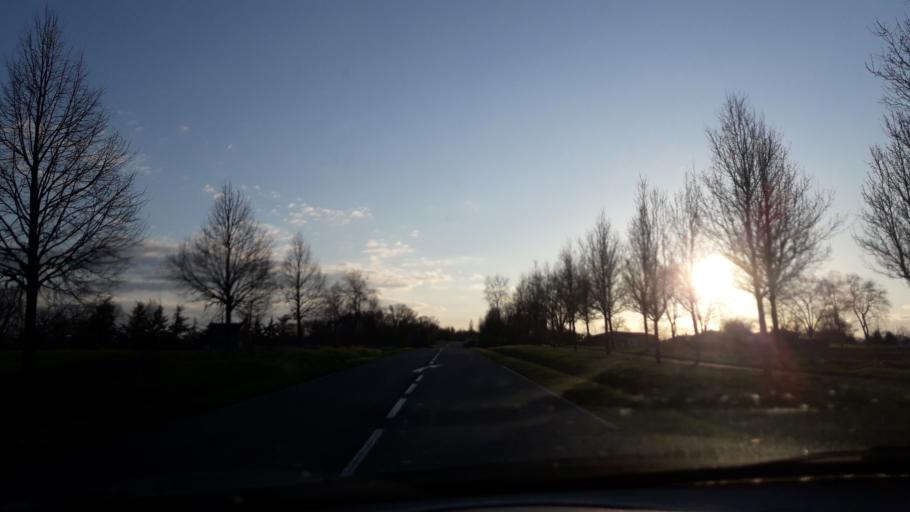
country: FR
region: Midi-Pyrenees
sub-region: Departement de la Haute-Garonne
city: Levignac
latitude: 43.6407
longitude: 1.1574
